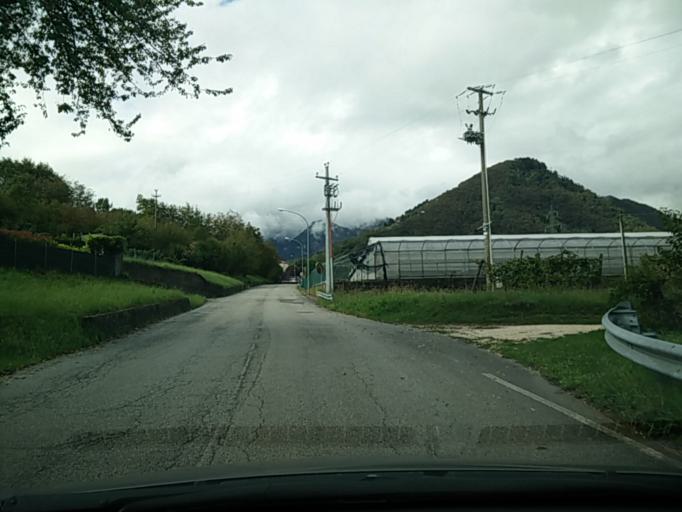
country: IT
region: Veneto
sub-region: Provincia di Belluno
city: Quero
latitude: 45.9237
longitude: 11.9397
